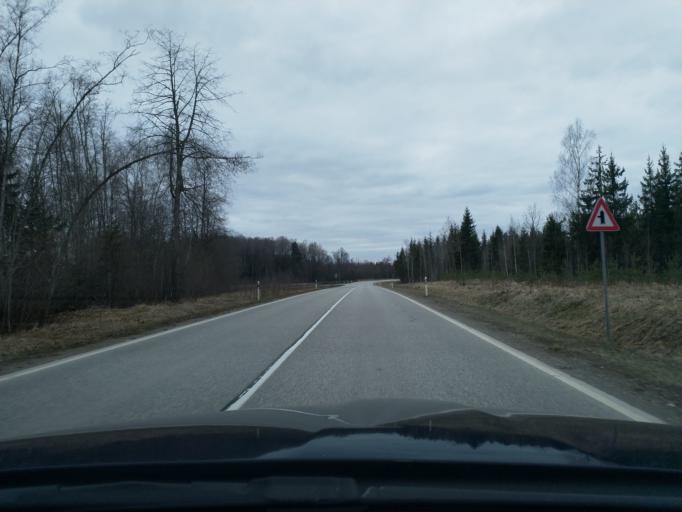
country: LV
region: Kuldigas Rajons
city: Kuldiga
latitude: 56.9576
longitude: 22.1141
